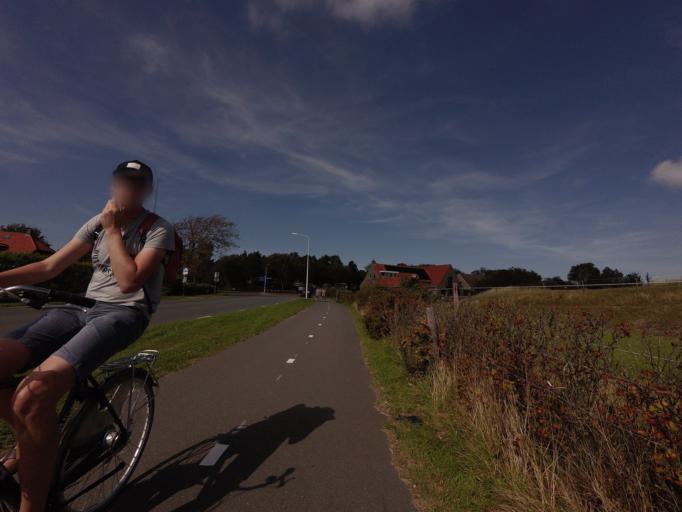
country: NL
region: Friesland
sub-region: Gemeente Ameland
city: Nes
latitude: 53.4452
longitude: 5.7647
